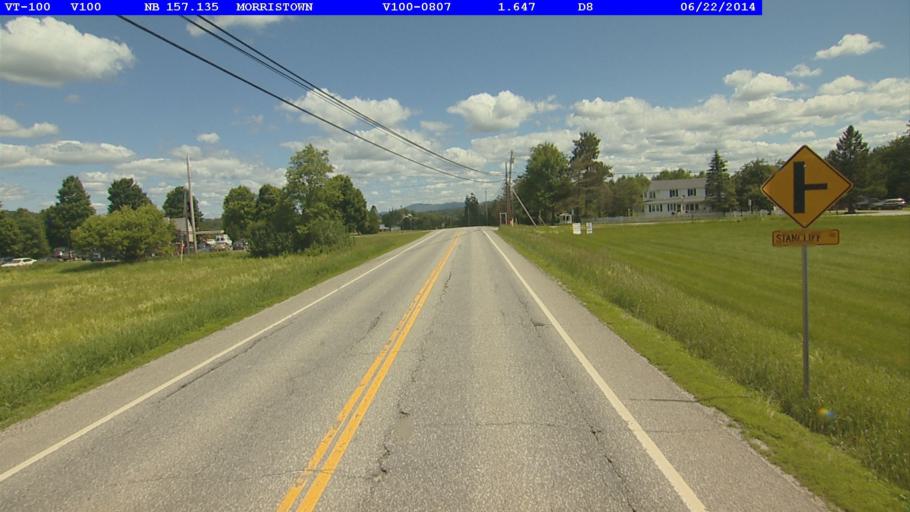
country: US
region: Vermont
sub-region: Lamoille County
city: Morristown
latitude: 44.5162
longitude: -72.6216
